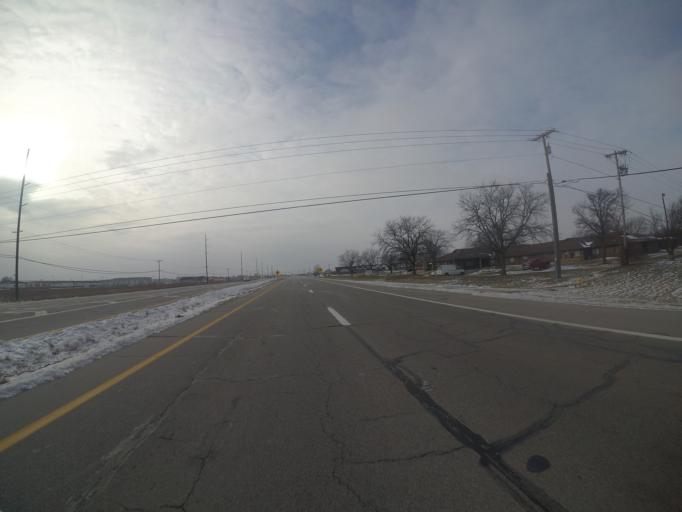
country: US
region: Ohio
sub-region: Wood County
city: Walbridge
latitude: 41.5639
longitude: -83.5324
